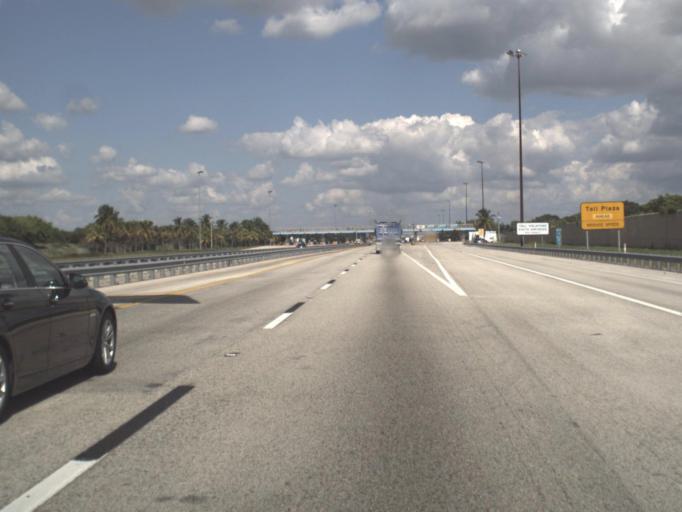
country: US
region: Florida
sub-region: Palm Beach County
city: Seminole Manor
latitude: 26.5590
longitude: -80.1729
